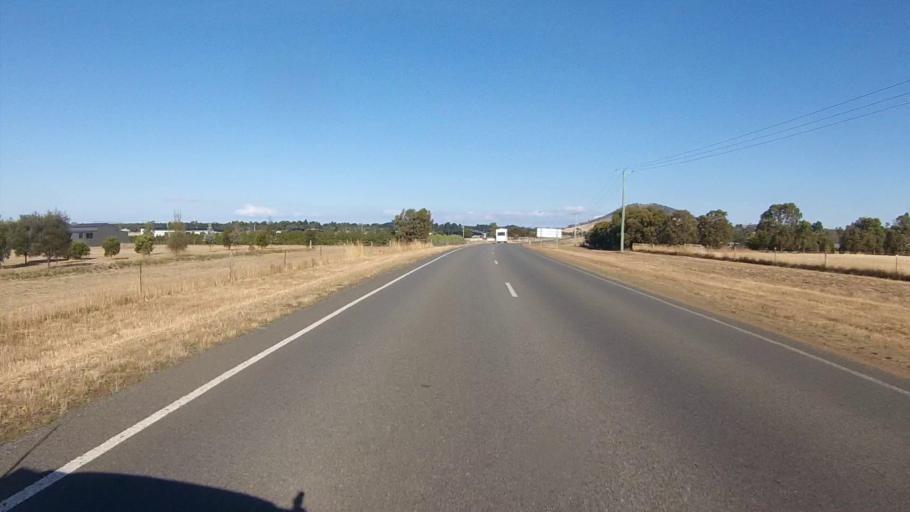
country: AU
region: Tasmania
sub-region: Clarence
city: Seven Mile Beach
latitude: -42.8472
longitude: 147.4808
